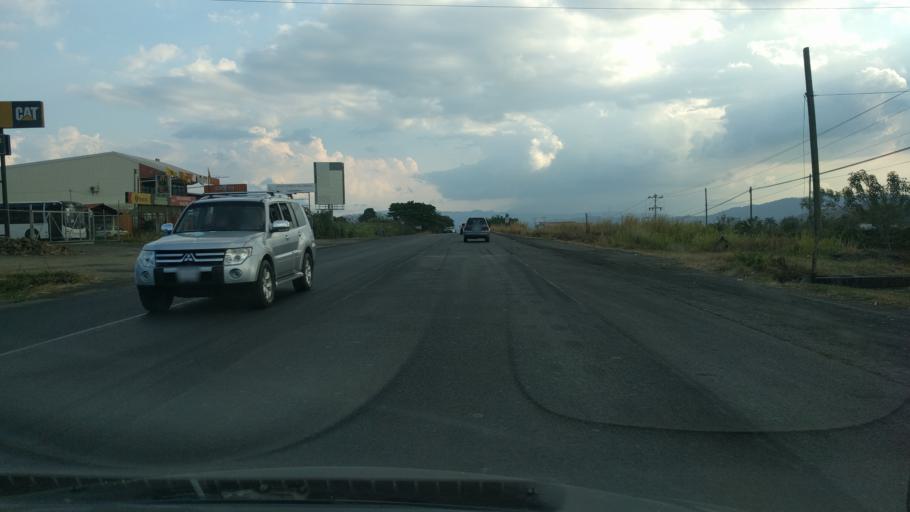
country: CR
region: Alajuela
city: Naranjo
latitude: 10.0487
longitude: -84.3618
